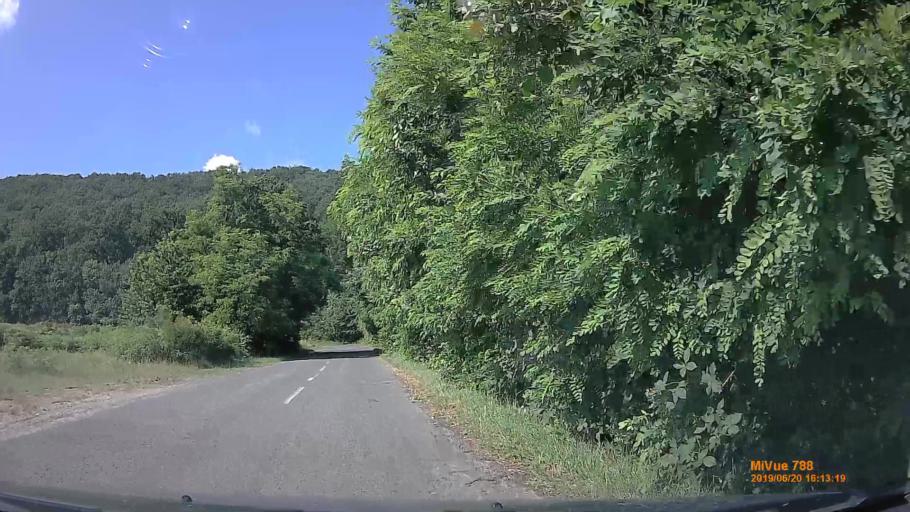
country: HU
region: Baranya
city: Pellerd
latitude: 46.0999
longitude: 18.0909
